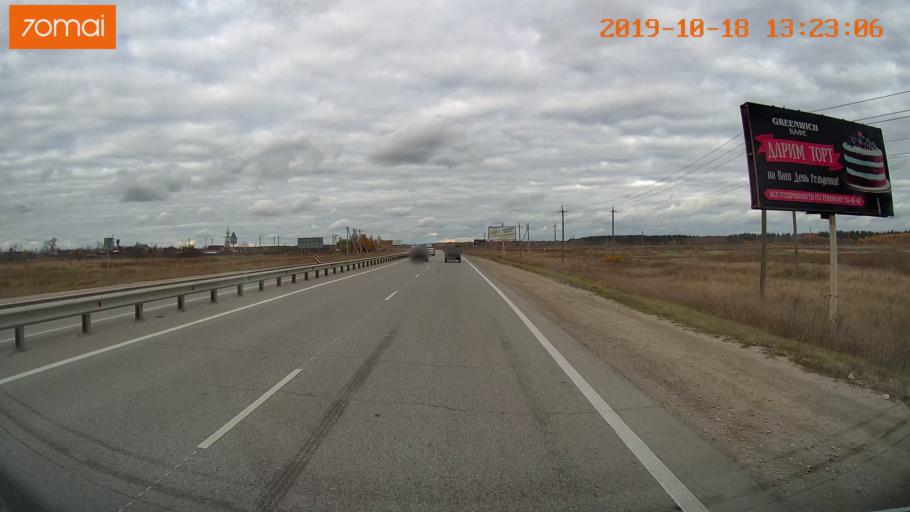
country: RU
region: Rjazan
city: Polyany
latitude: 54.7102
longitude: 39.8474
